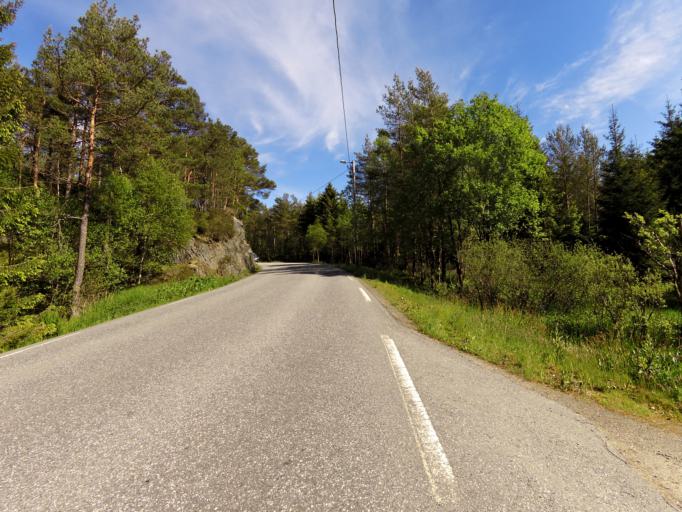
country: NO
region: Hordaland
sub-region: Stord
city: Sagvag
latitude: 59.7906
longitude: 5.4341
